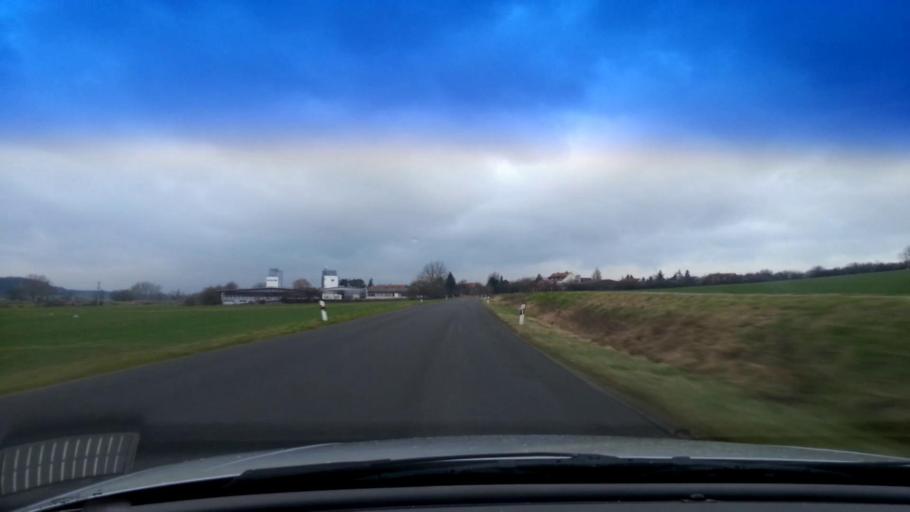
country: DE
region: Bavaria
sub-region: Upper Franconia
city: Burgebrach
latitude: 49.8349
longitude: 10.7687
